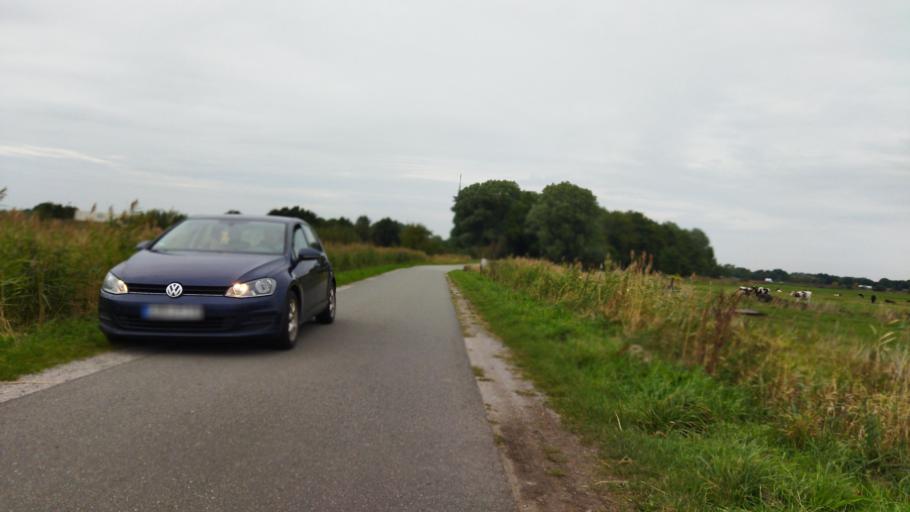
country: DE
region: Lower Saxony
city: Leer
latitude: 53.2528
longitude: 7.4378
